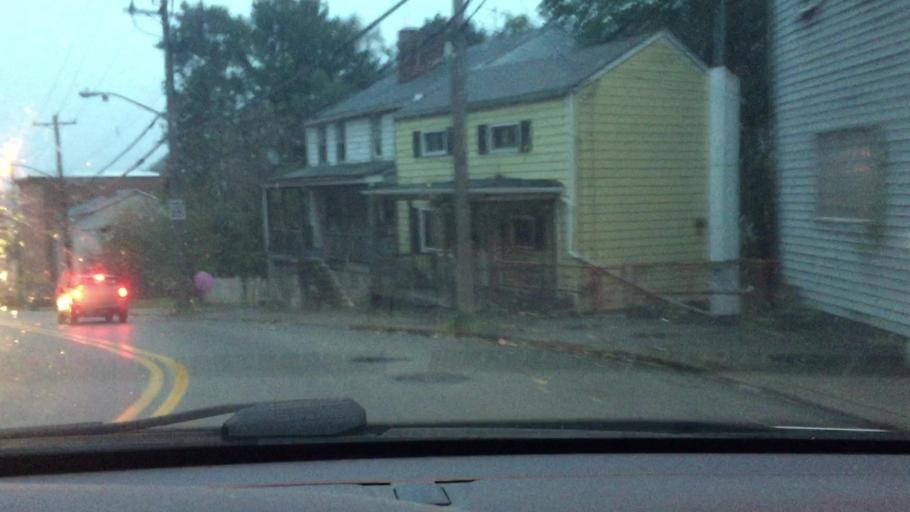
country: US
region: Pennsylvania
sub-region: Allegheny County
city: Crafton
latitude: 40.4413
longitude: -80.0366
